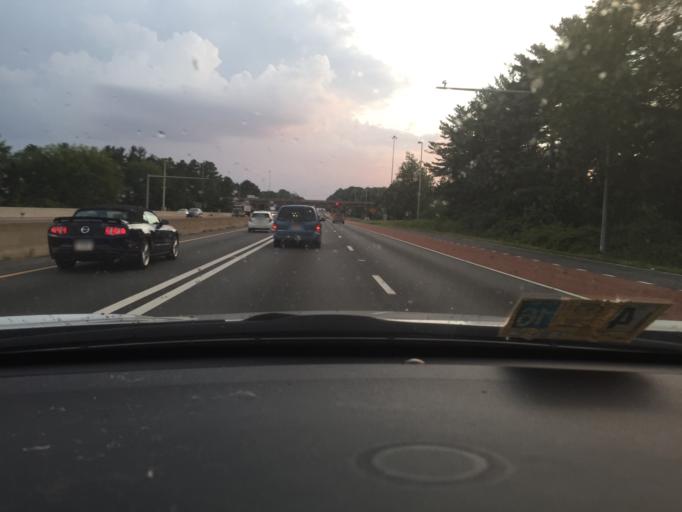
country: US
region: Virginia
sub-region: Fairfax County
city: Oakton
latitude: 38.8693
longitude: -77.3061
